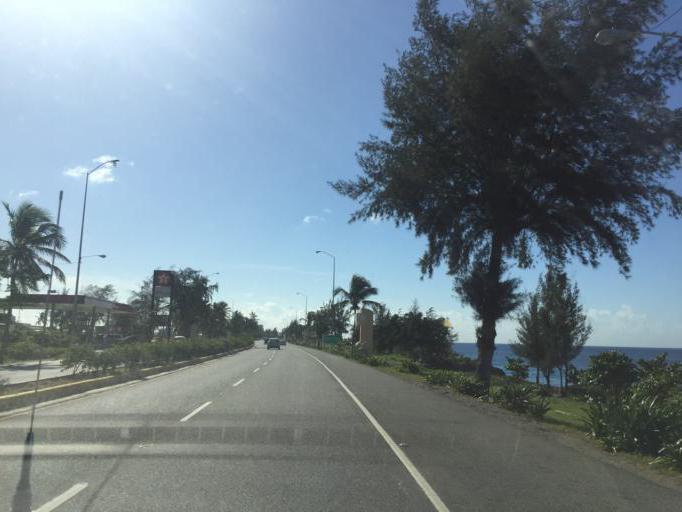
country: DO
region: Santo Domingo
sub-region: Santo Domingo
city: Boca Chica
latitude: 18.4374
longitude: -69.6814
